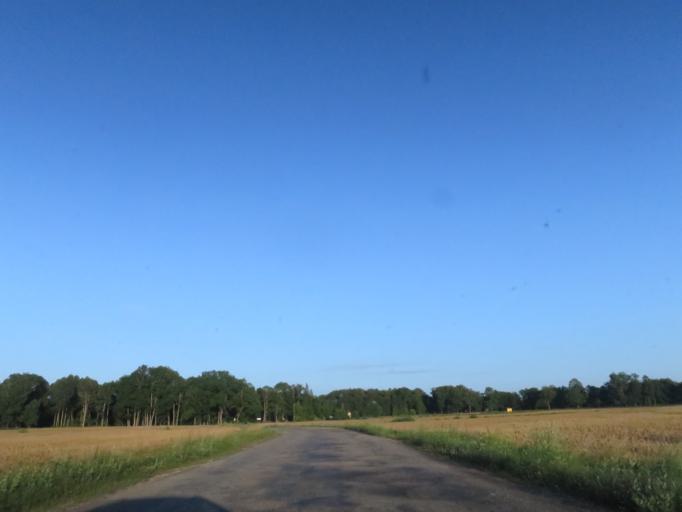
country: LV
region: Sigulda
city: Sigulda
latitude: 57.1712
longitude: 24.8207
